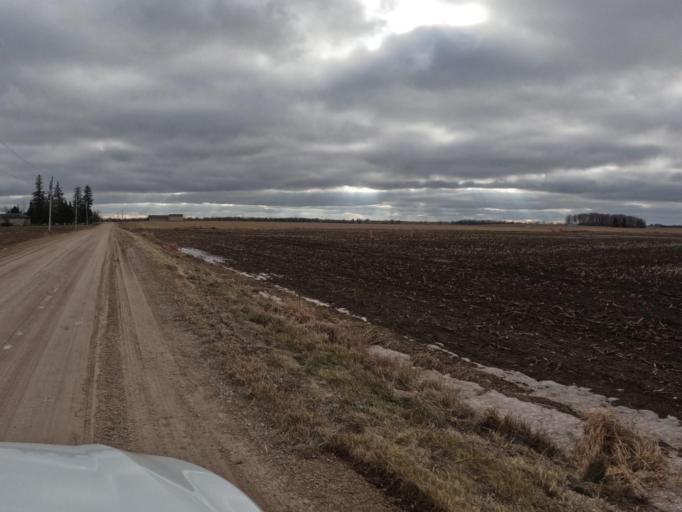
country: CA
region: Ontario
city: Shelburne
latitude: 43.8673
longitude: -80.4012
